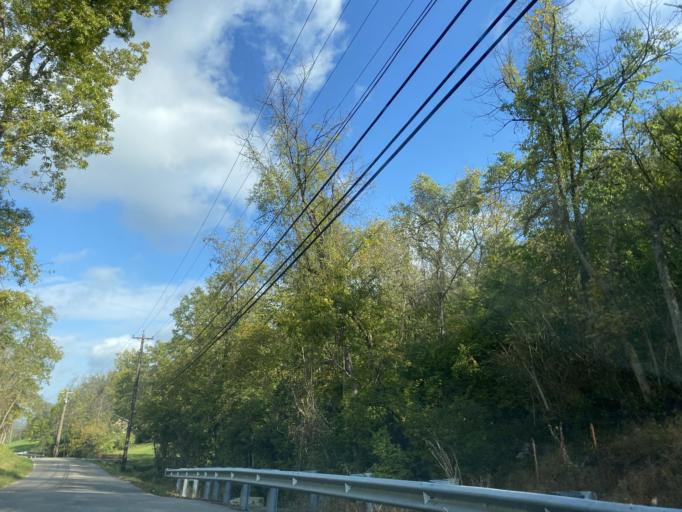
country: US
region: Kentucky
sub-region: Campbell County
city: Cold Spring
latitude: 39.0311
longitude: -84.4187
